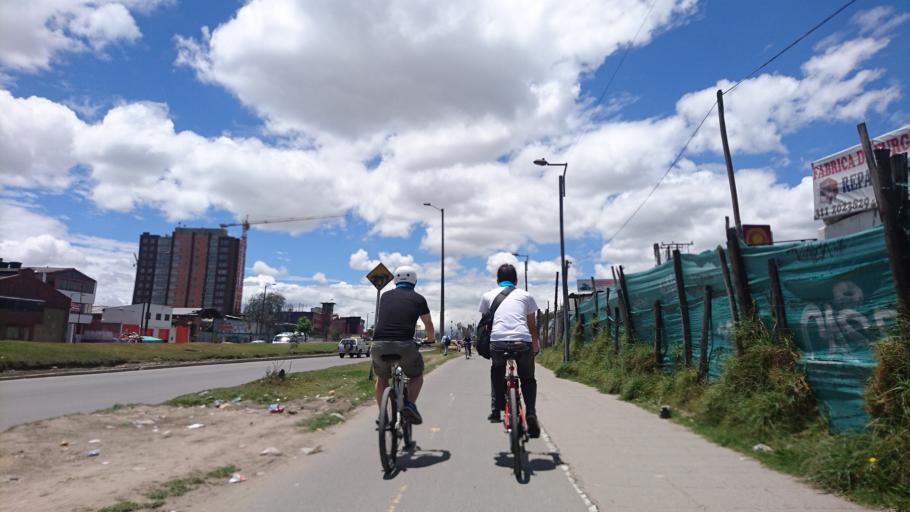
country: CO
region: Bogota D.C.
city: Bogota
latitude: 4.6566
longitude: -74.1391
